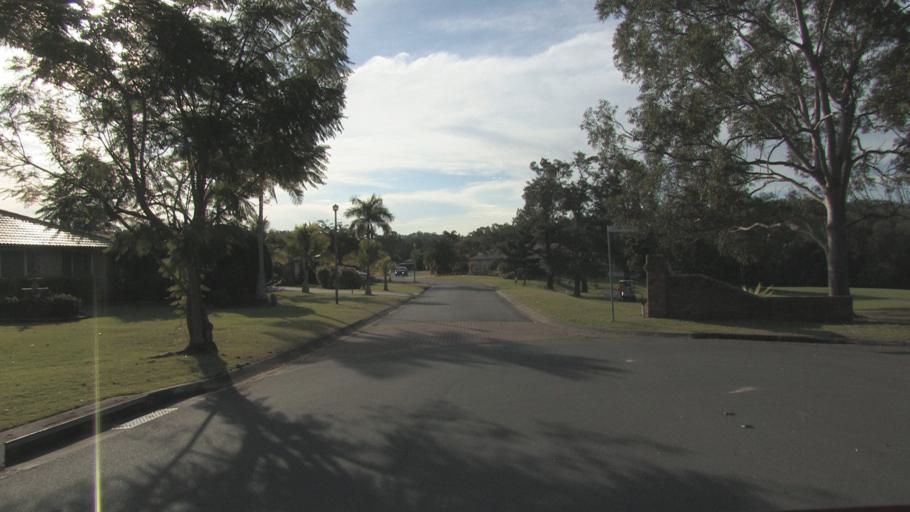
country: AU
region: Queensland
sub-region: Logan
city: Windaroo
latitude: -27.7396
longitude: 153.1979
